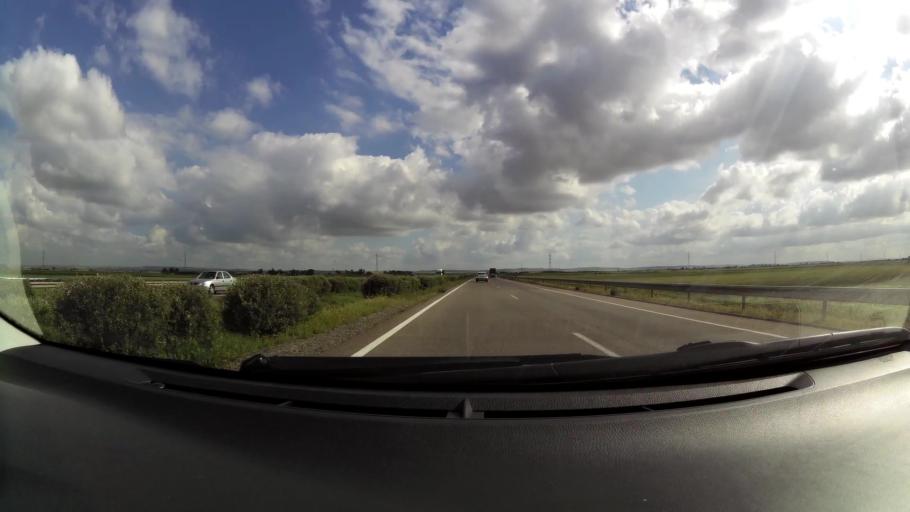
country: MA
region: Chaouia-Ouardigha
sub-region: Settat Province
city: Berrechid
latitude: 33.1625
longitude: -7.5704
